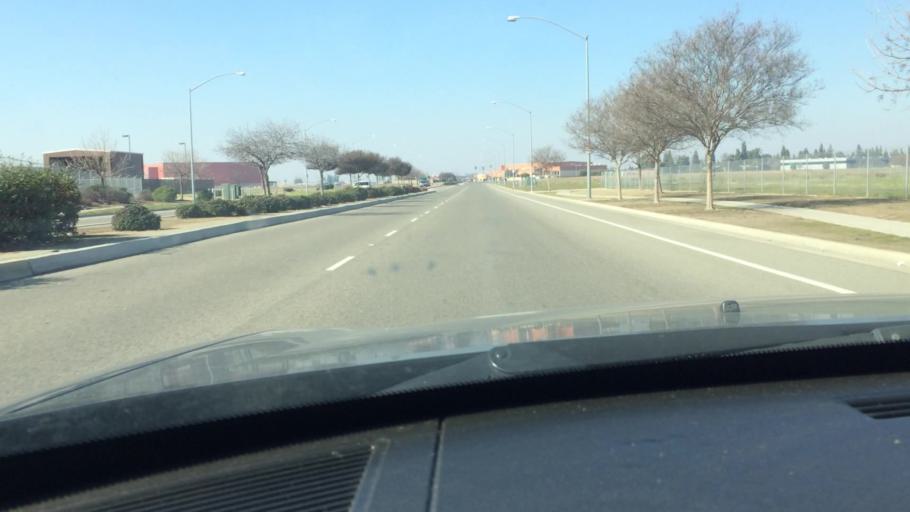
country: US
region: California
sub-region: Fresno County
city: Tarpey Village
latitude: 36.7817
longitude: -119.7131
